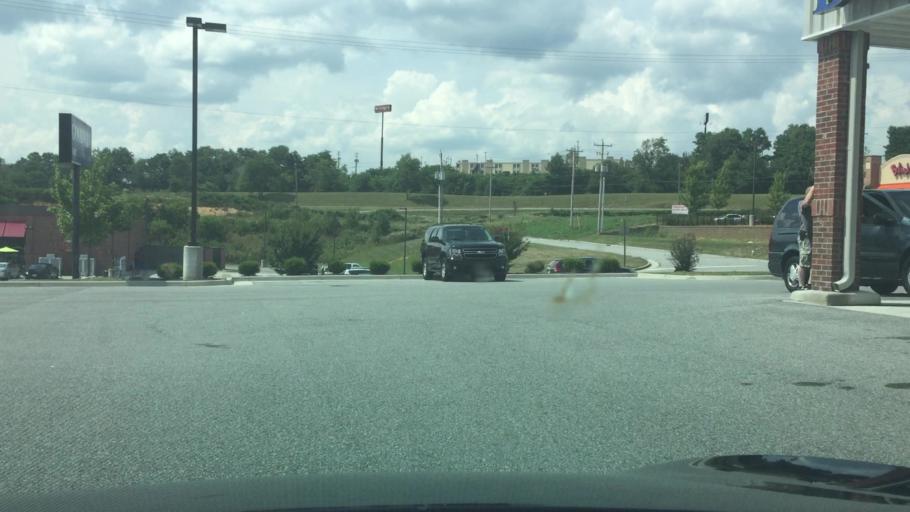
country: US
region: Virginia
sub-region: Wythe County
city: Wytheville
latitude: 36.9589
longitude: -81.0946
